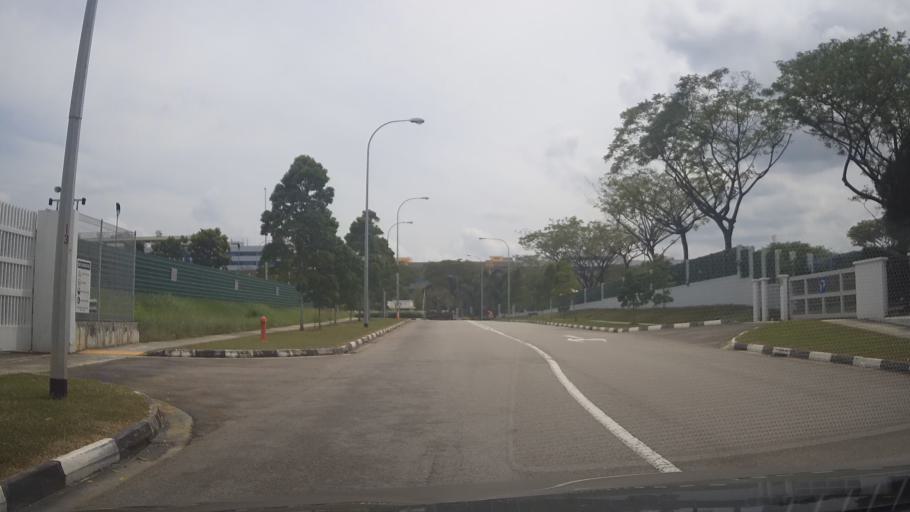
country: MY
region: Johor
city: Johor Bahru
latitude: 1.4567
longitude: 103.7946
